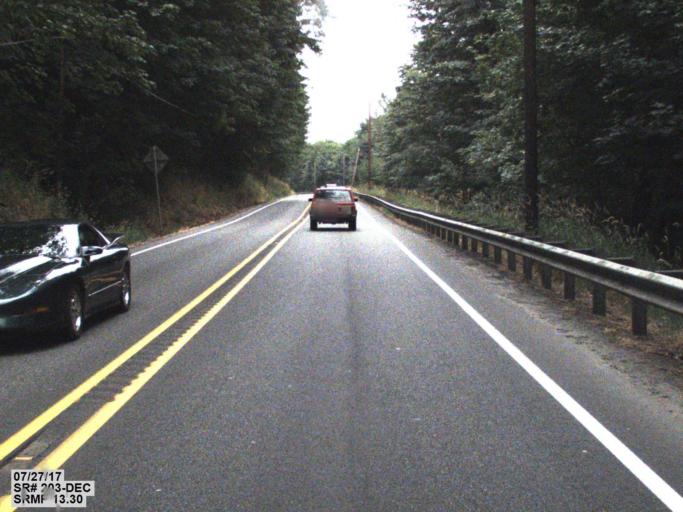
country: US
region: Washington
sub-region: King County
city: Duvall
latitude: 47.7186
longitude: -121.9859
